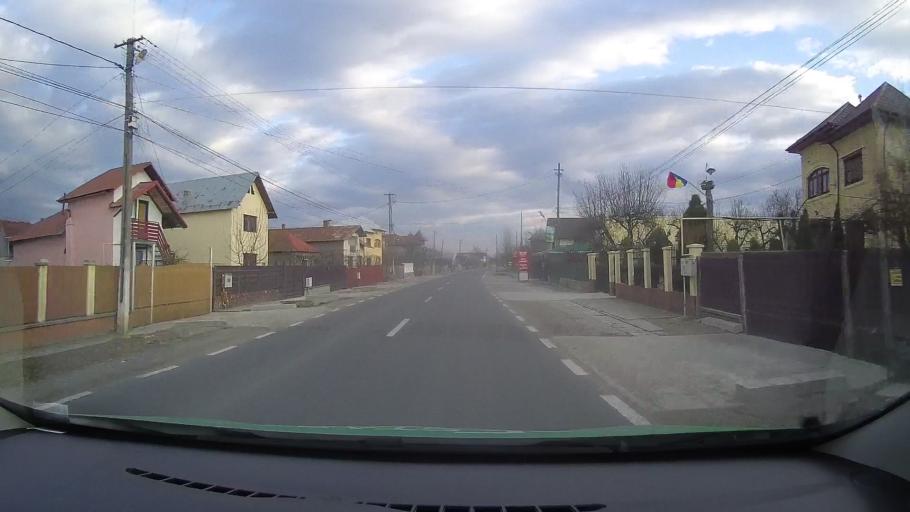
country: RO
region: Dambovita
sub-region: Comuna I. L. Caragiale
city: Ghirdoveni
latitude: 44.9292
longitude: 25.6886
